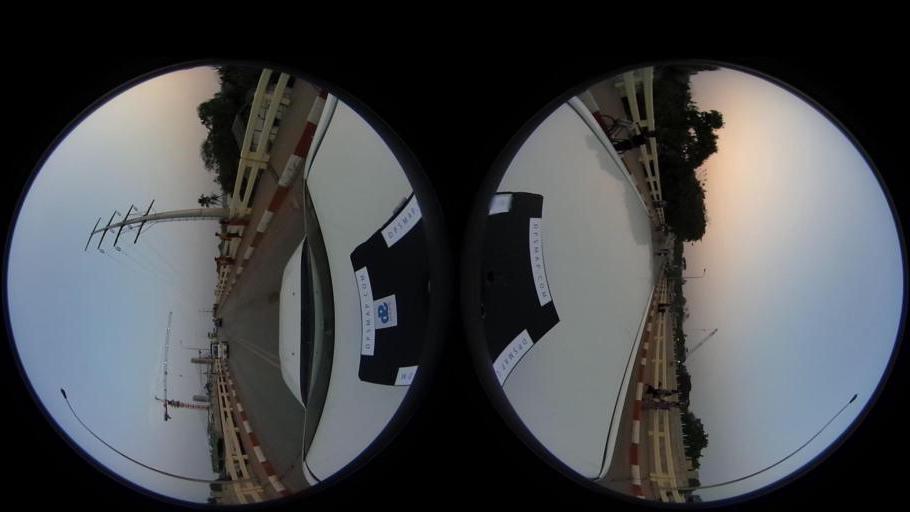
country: MM
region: Yangon
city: Yangon
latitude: 16.7859
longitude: 96.1782
